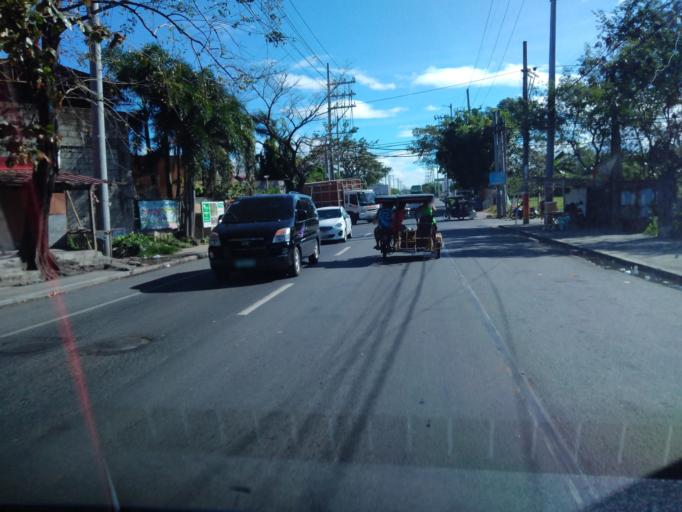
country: PH
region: Central Luzon
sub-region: Province of Bulacan
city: Santa Maria
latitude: 14.8304
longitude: 120.9632
